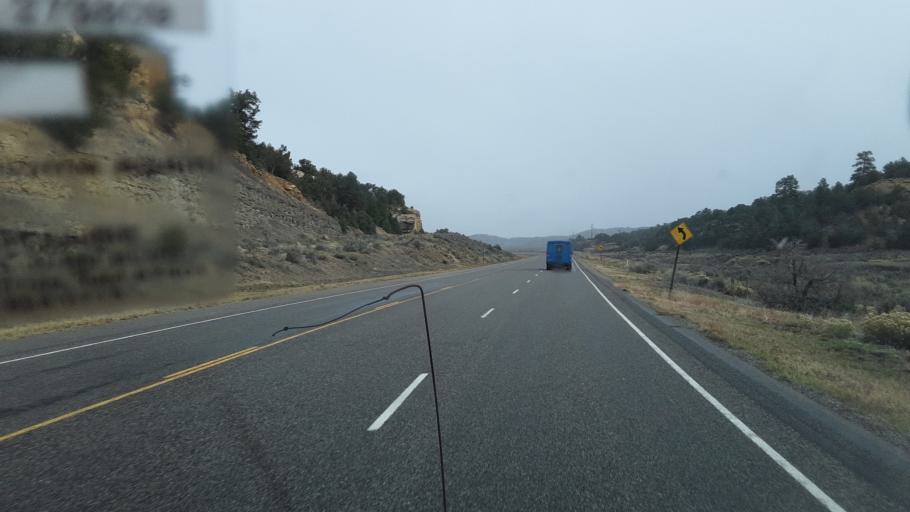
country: US
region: New Mexico
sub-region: Rio Arriba County
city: Tierra Amarilla
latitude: 36.4325
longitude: -106.4768
